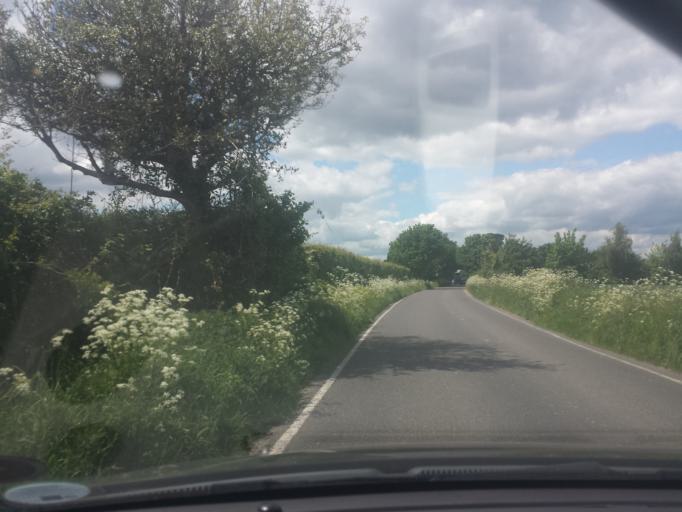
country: GB
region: England
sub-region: Essex
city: Little Clacton
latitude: 51.8887
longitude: 1.1546
